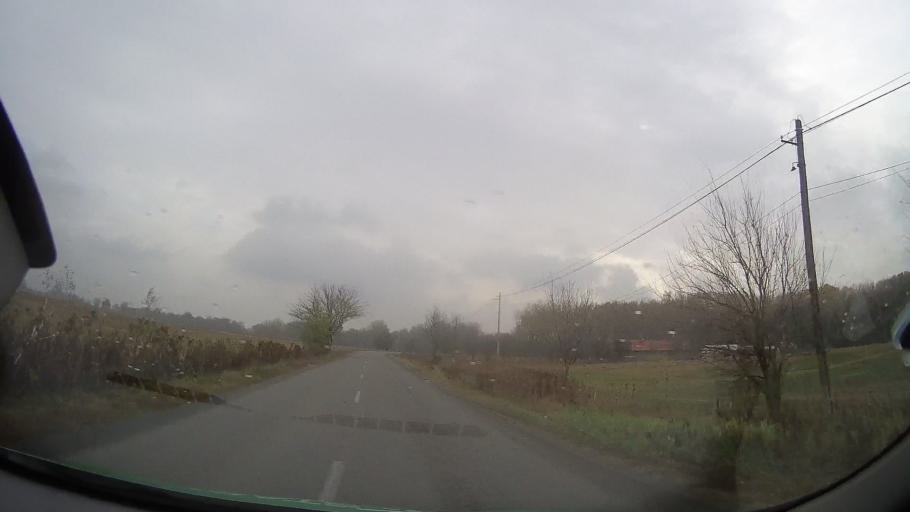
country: RO
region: Prahova
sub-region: Comuna Gherghita
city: Gherghita
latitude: 44.8143
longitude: 26.2684
